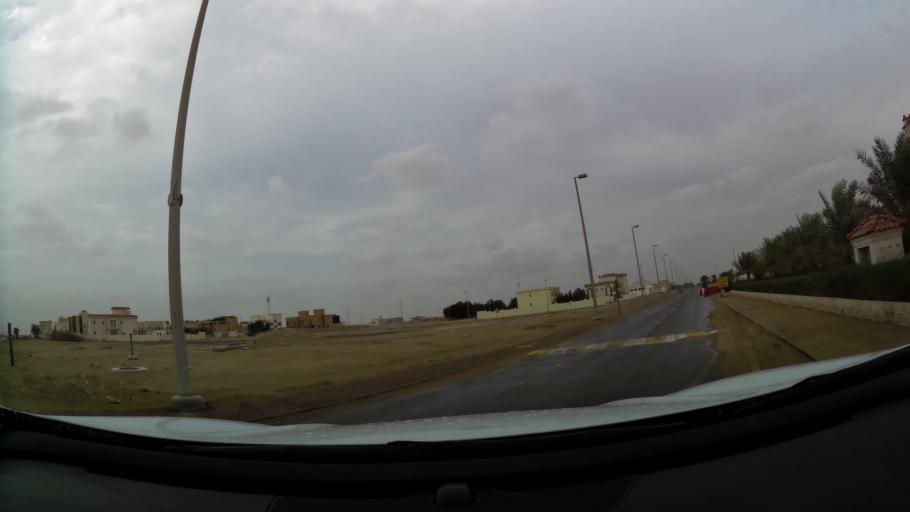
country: AE
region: Abu Dhabi
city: Abu Dhabi
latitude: 24.3542
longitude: 54.6183
